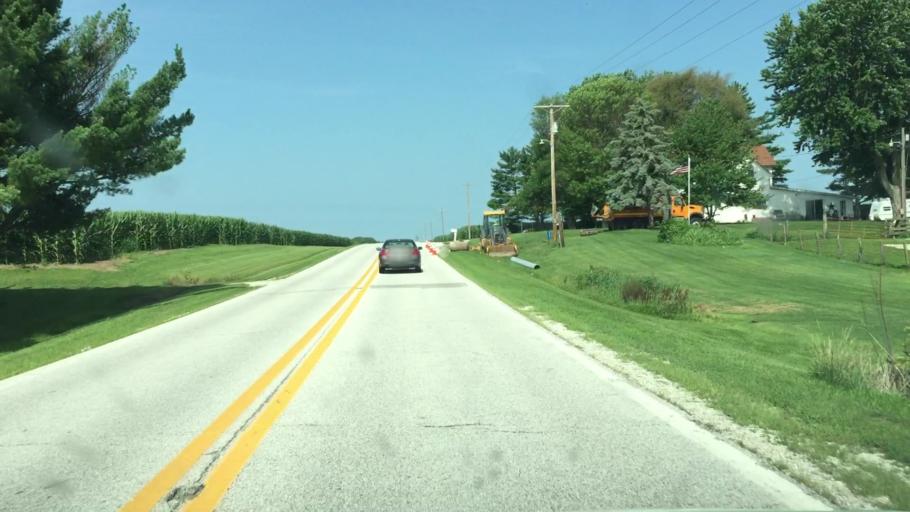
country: US
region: Illinois
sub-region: Hancock County
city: Nauvoo
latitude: 40.5519
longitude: -91.3388
